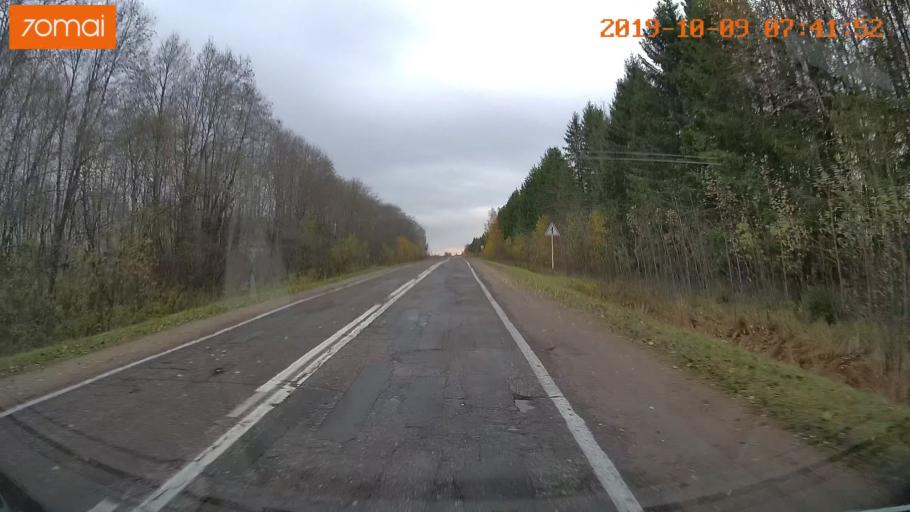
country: RU
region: Jaroslavl
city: Kukoboy
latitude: 58.6405
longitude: 39.7132
